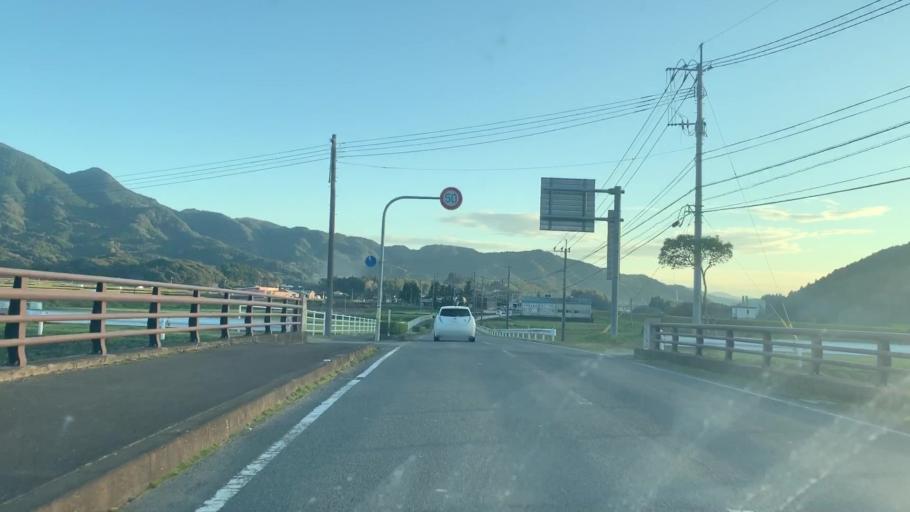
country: JP
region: Saga Prefecture
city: Imaricho-ko
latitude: 33.2994
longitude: 129.9699
